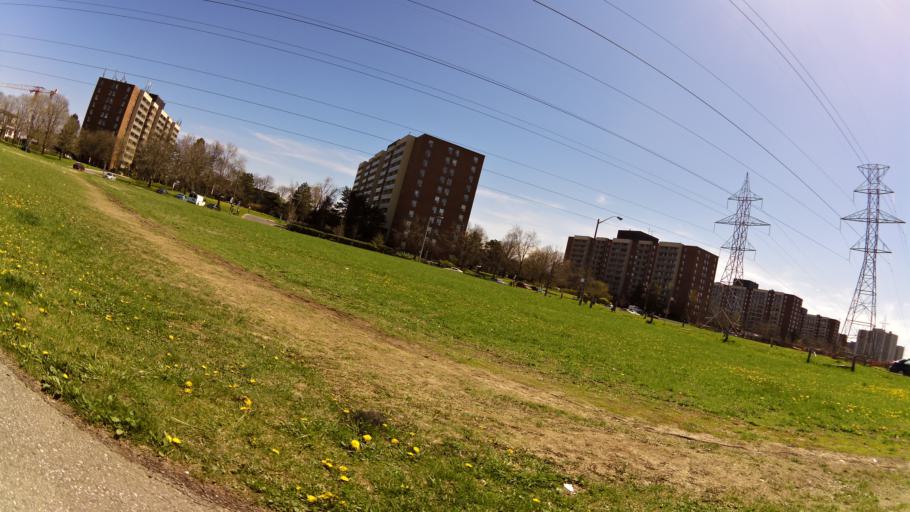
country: CA
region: Ontario
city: Concord
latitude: 43.7660
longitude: -79.4940
